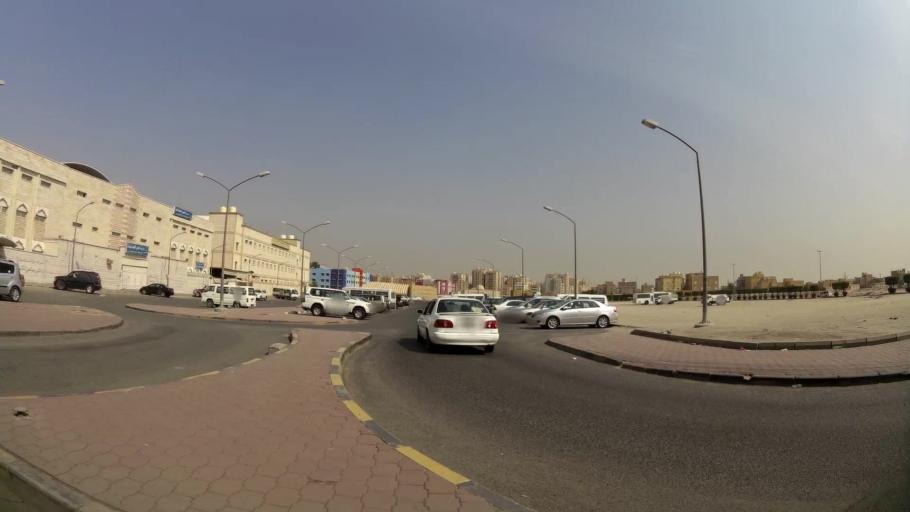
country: KW
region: Al Farwaniyah
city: Al Farwaniyah
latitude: 29.2510
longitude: 47.9287
